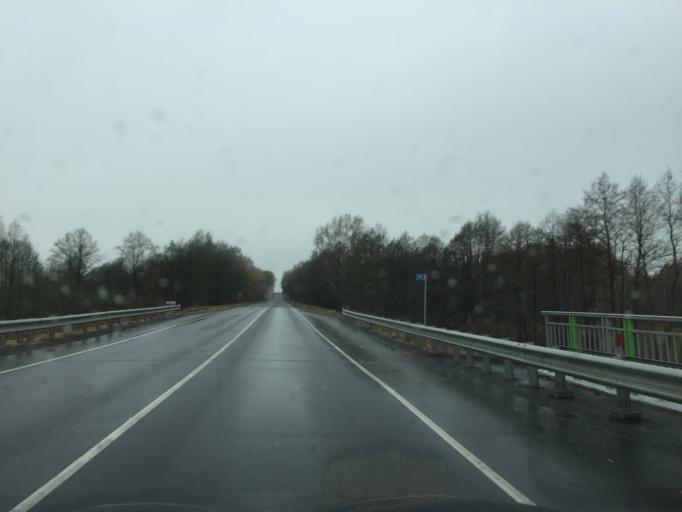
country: BY
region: Gomel
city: Karma
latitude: 53.3392
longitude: 30.7994
